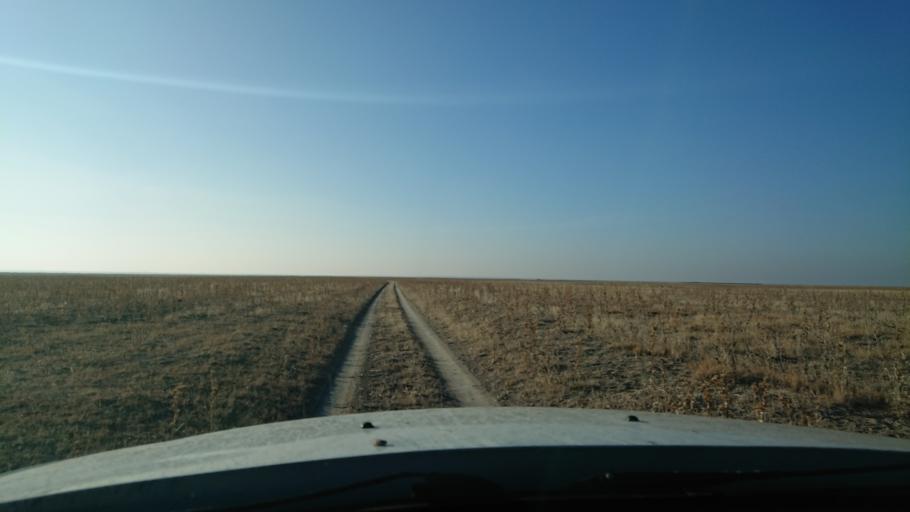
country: TR
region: Aksaray
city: Sultanhani
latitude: 38.3717
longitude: 33.5461
